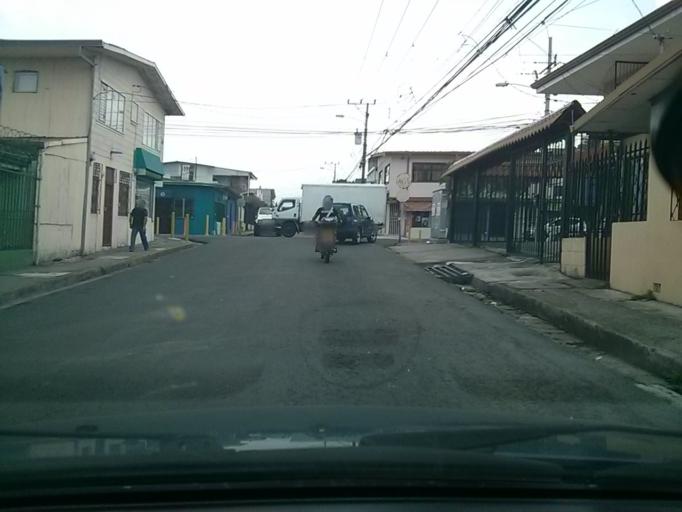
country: CR
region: San Jose
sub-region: Canton de Goicoechea
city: Guadalupe
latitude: 9.9454
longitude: -84.0523
